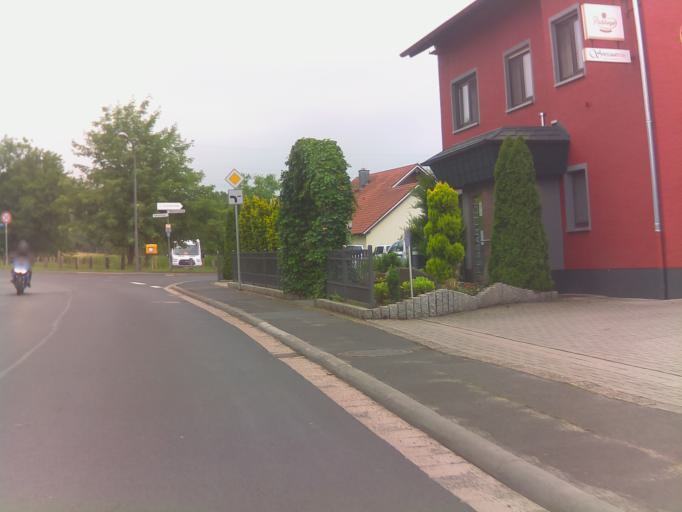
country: DE
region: Hesse
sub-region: Regierungsbezirk Darmstadt
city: Bad Soden-Salmunster
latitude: 50.2711
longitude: 9.3799
